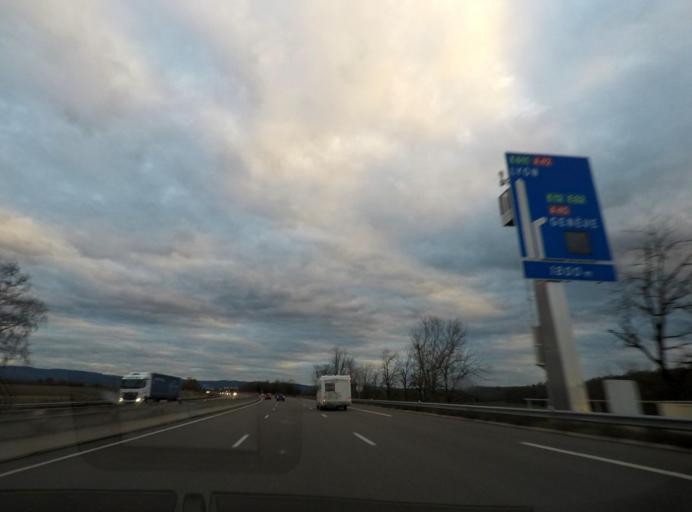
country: FR
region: Rhone-Alpes
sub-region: Departement de l'Ain
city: Saint-Martin-du-Mont
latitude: 46.0798
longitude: 5.2950
